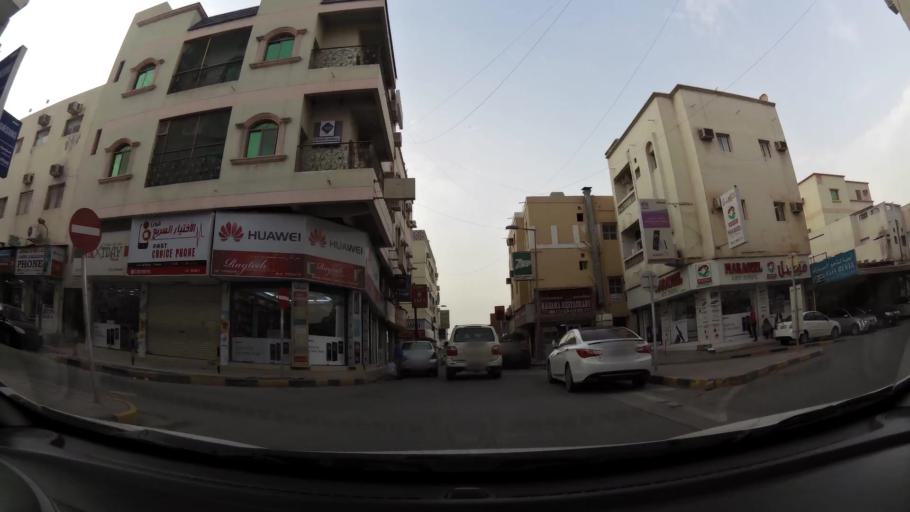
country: BH
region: Northern
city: Ar Rifa'
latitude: 26.1209
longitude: 50.5679
